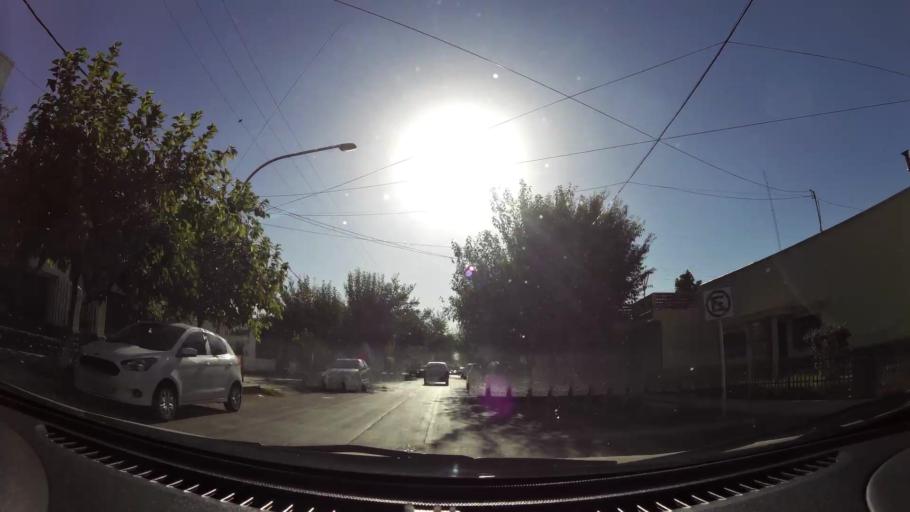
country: AR
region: Mendoza
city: Mendoza
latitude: -32.9001
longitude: -68.8106
